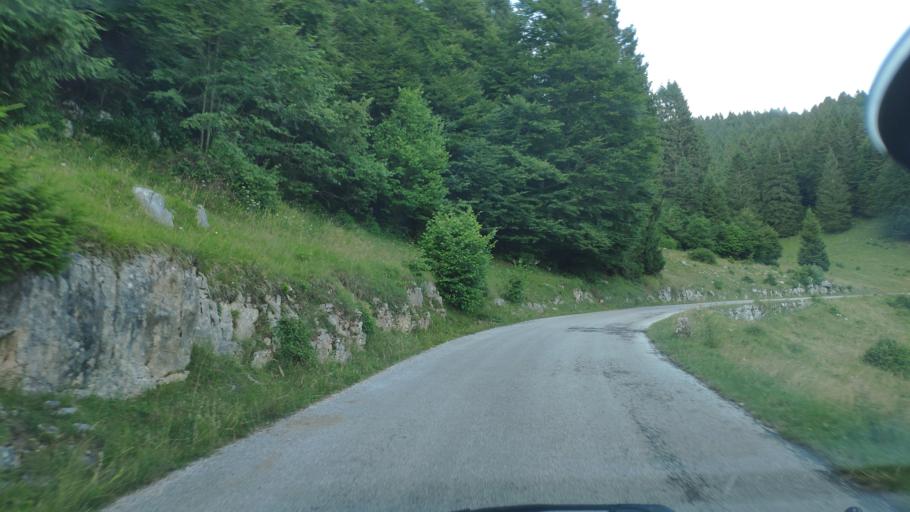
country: IT
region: Veneto
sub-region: Provincia di Vicenza
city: Calvene
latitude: 45.7989
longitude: 11.5071
